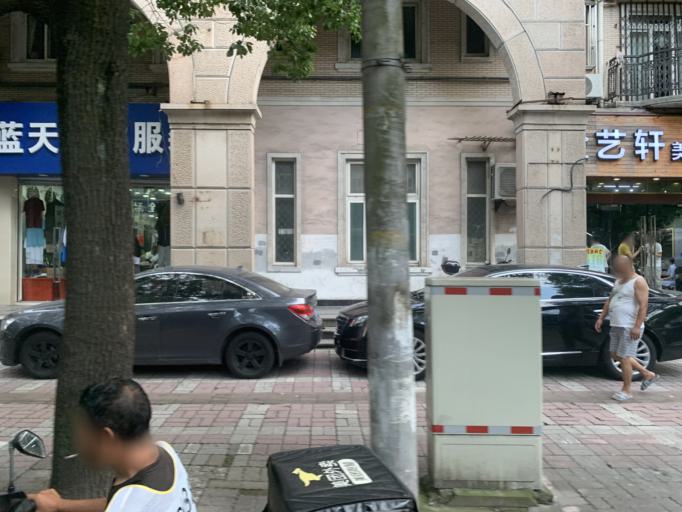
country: CN
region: Shanghai Shi
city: Pudong
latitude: 31.2473
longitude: 121.5499
